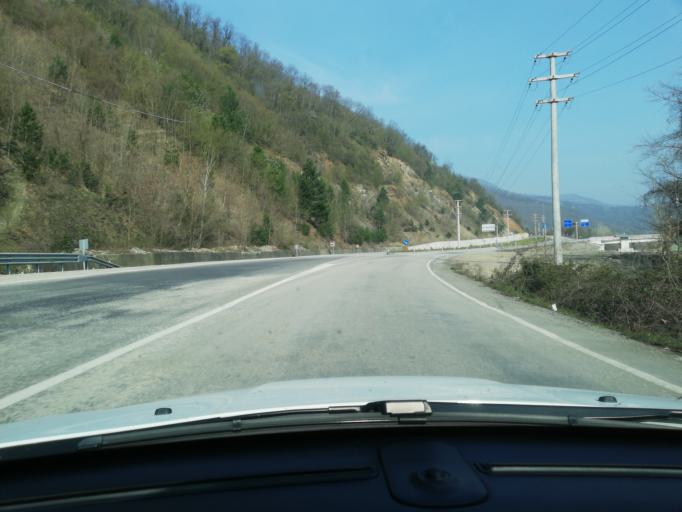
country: TR
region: Karabuk
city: Yenice
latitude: 41.2042
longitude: 32.3668
